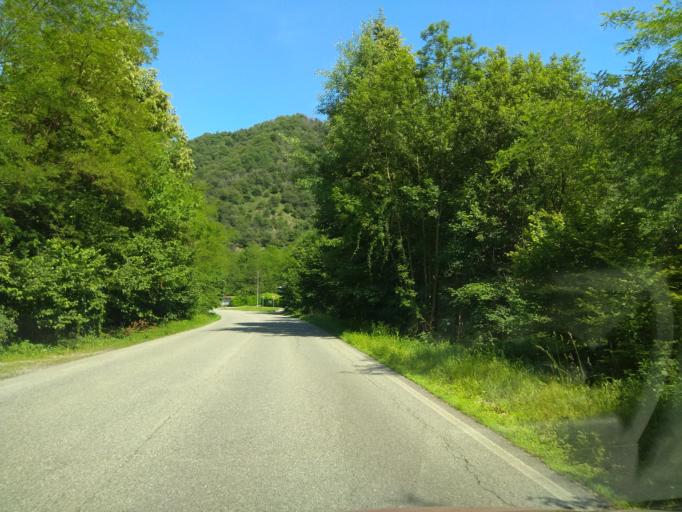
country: IT
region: Piedmont
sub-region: Provincia di Biella
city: Pray
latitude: 45.6740
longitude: 8.2284
